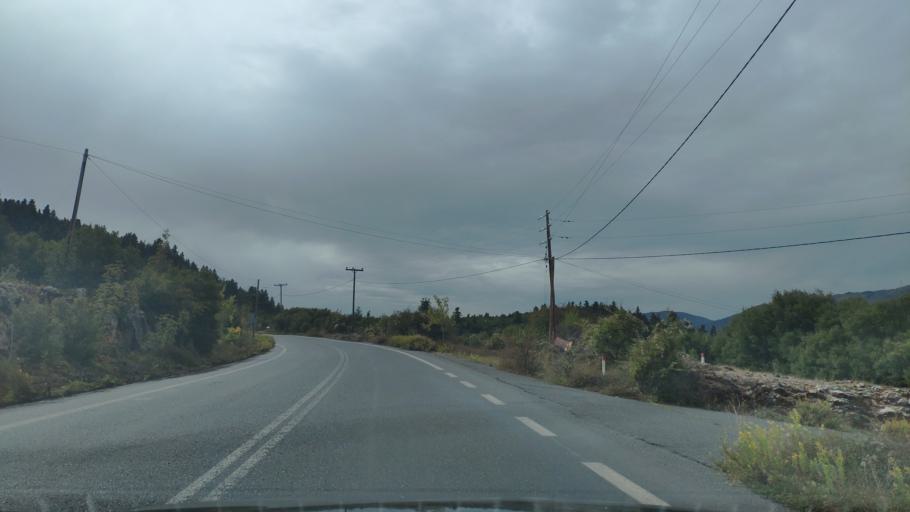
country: GR
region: Peloponnese
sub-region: Nomos Arkadias
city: Langadhia
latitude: 37.6656
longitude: 22.1928
